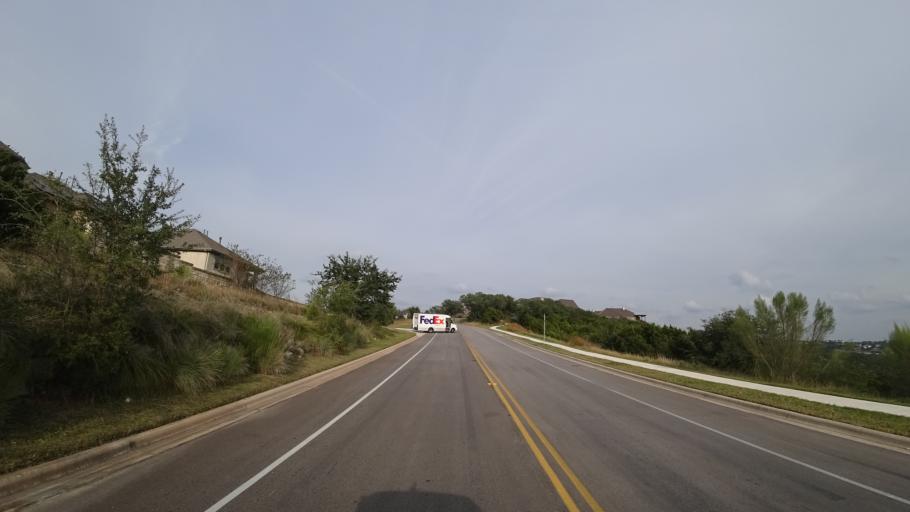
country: US
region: Texas
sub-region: Travis County
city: Hudson Bend
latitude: 30.3780
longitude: -97.8793
